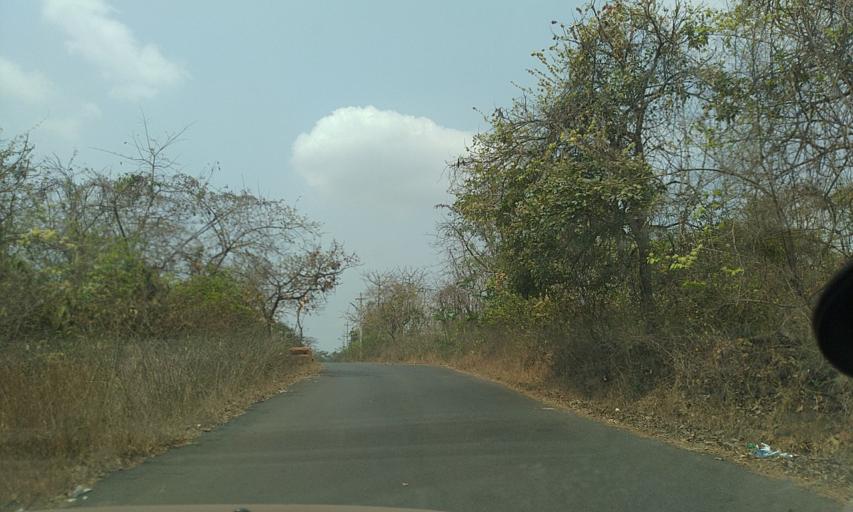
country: IN
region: Goa
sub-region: North Goa
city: Goa Velha
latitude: 15.4846
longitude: 73.8994
